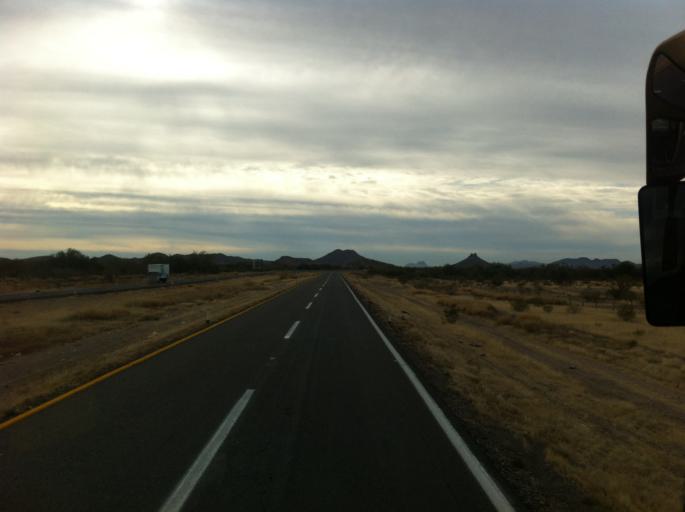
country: MX
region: Sonora
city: Hermosillo
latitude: 28.9362
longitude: -110.9564
